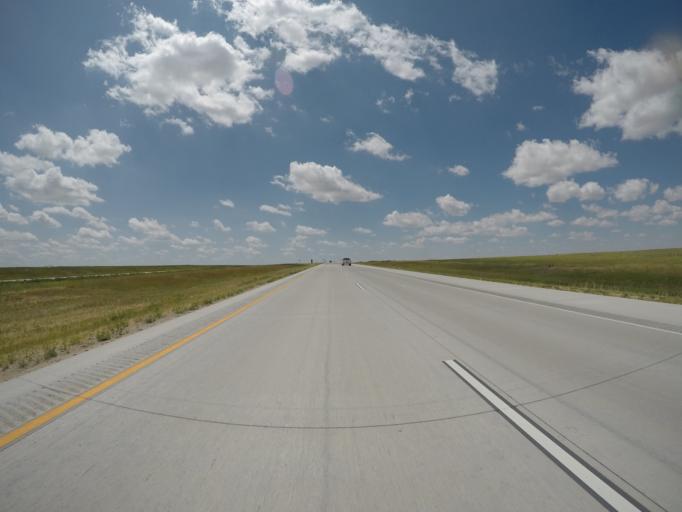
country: US
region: Colorado
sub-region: Kit Carson County
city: Burlington
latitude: 39.2943
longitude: -102.7832
